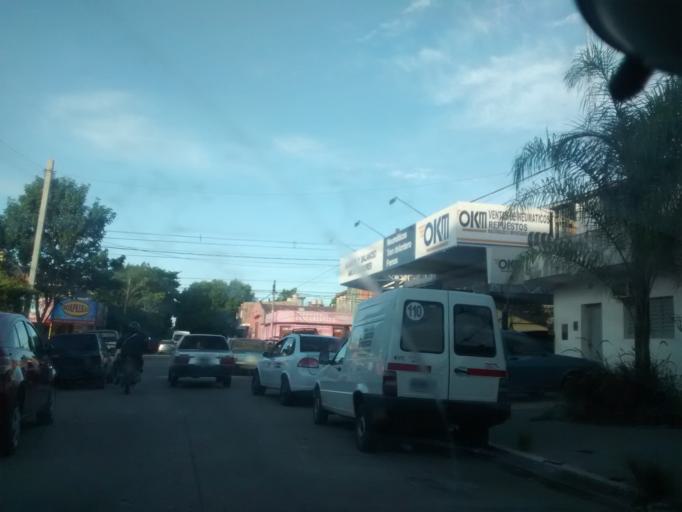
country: AR
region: Chaco
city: Resistencia
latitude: -27.4618
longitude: -58.9738
